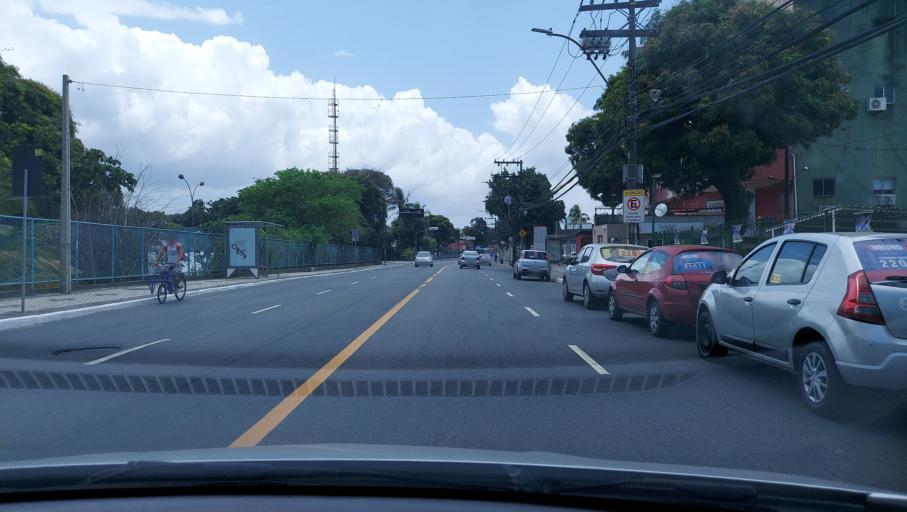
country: BR
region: Bahia
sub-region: Salvador
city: Salvador
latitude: -12.9639
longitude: -38.4722
